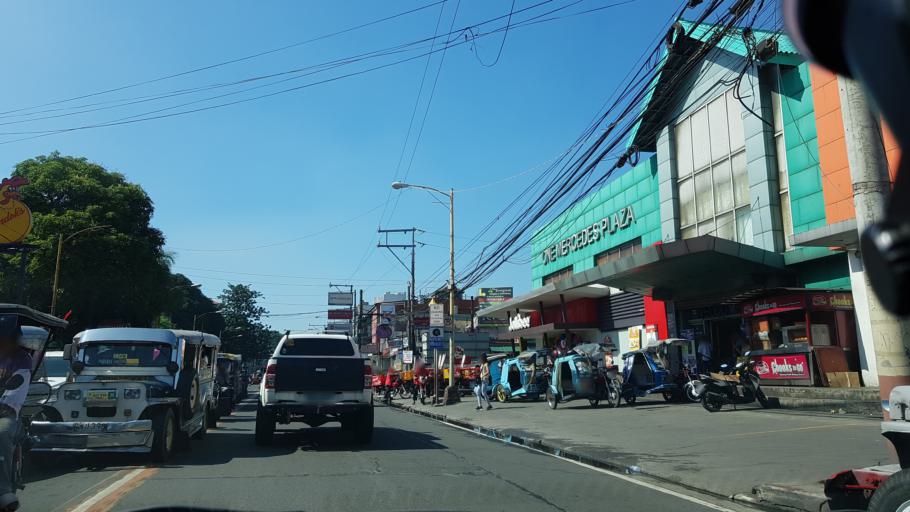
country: PH
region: Metro Manila
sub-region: Pasig
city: Pasig City
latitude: 14.5683
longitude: 121.0859
